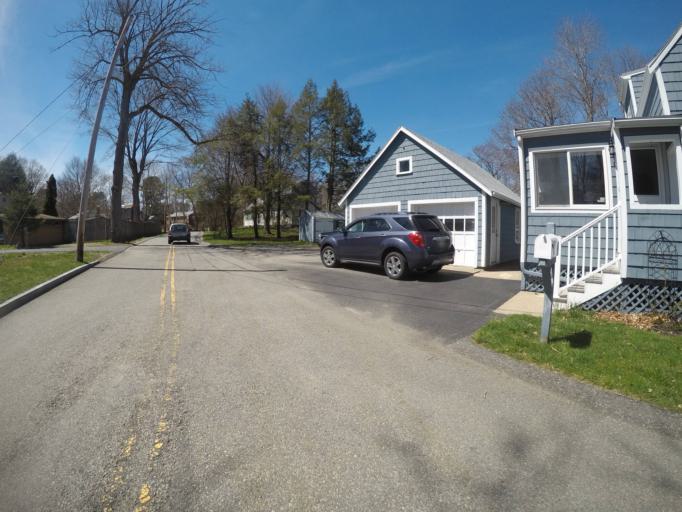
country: US
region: Massachusetts
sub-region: Bristol County
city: Easton
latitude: 42.0464
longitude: -71.0830
